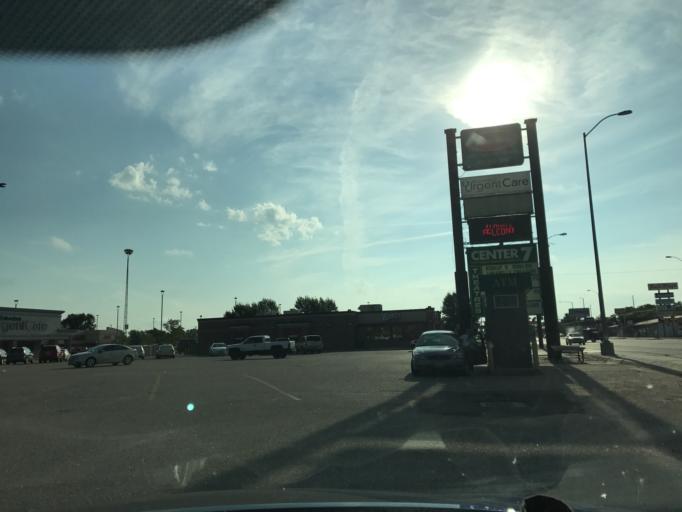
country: US
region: Nebraska
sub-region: Platte County
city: Columbus
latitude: 41.4389
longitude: -97.3662
